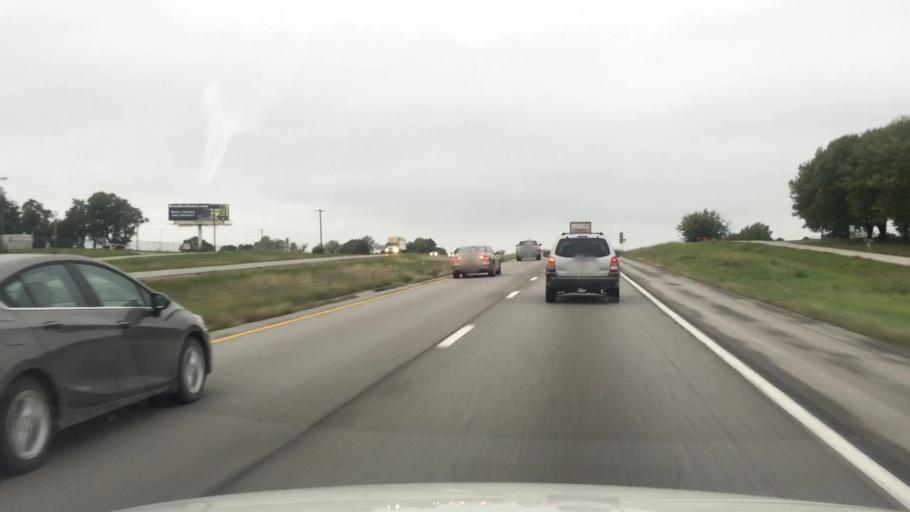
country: US
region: Missouri
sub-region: Jackson County
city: Oak Grove
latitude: 39.0169
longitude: -94.1494
